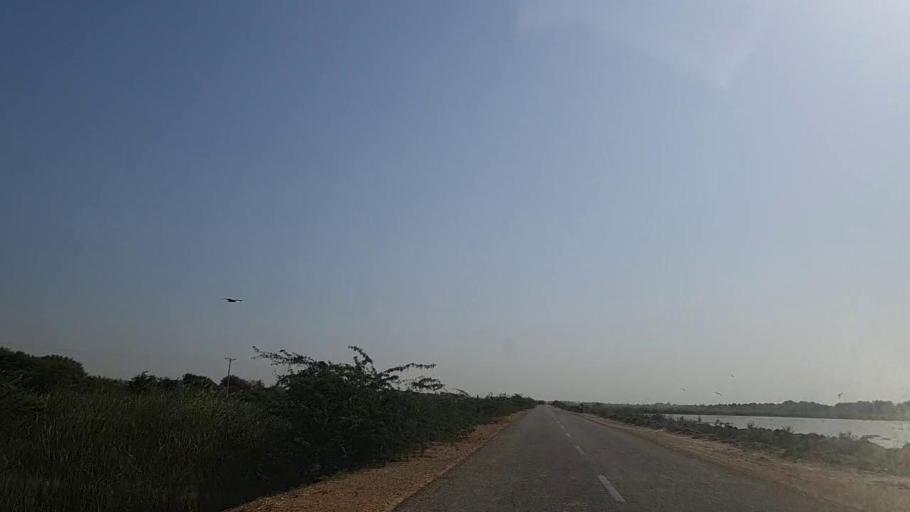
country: PK
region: Sindh
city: Jati
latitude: 24.5083
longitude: 68.2745
